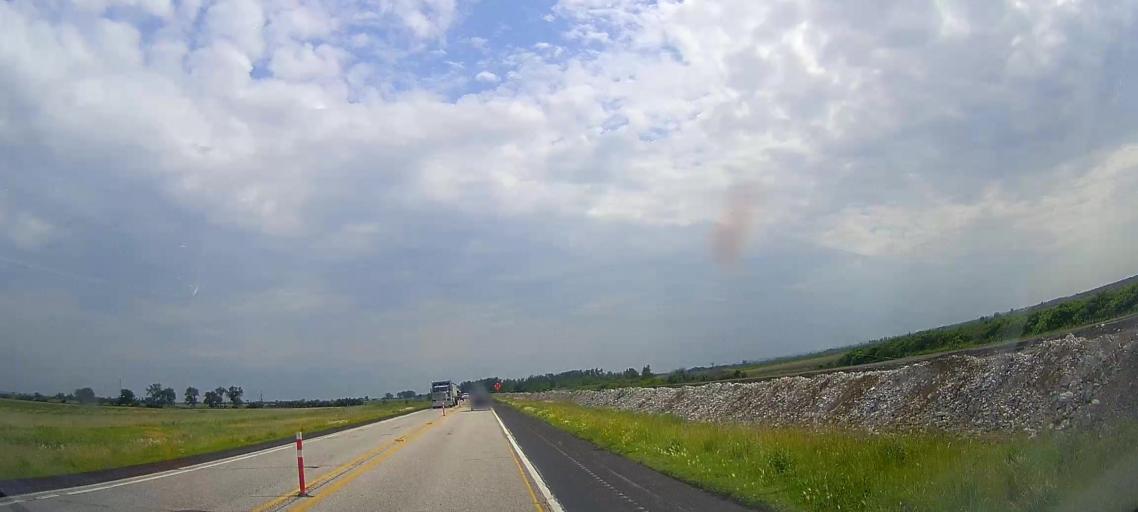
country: US
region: Nebraska
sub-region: Washington County
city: Blair
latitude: 41.6889
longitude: -96.0417
